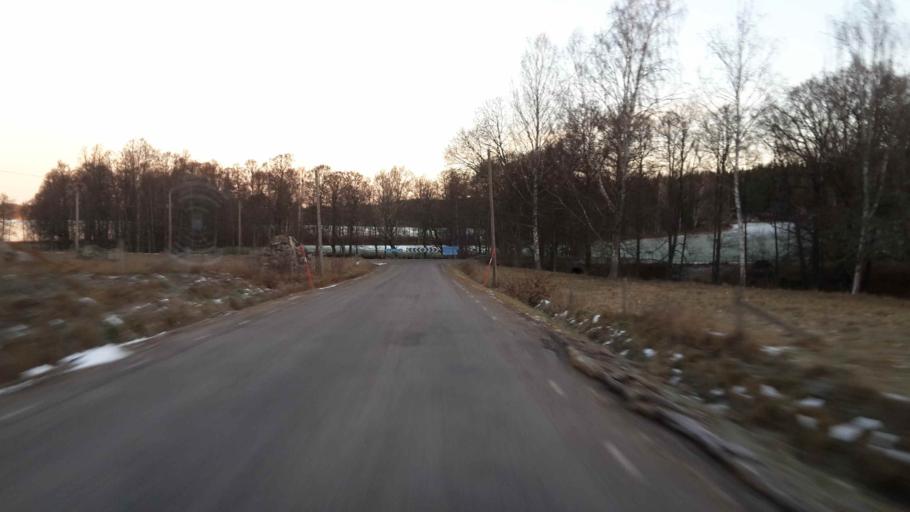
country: SE
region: OEstergoetland
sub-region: Atvidabergs Kommun
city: Atvidaberg
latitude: 58.2804
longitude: 16.1480
